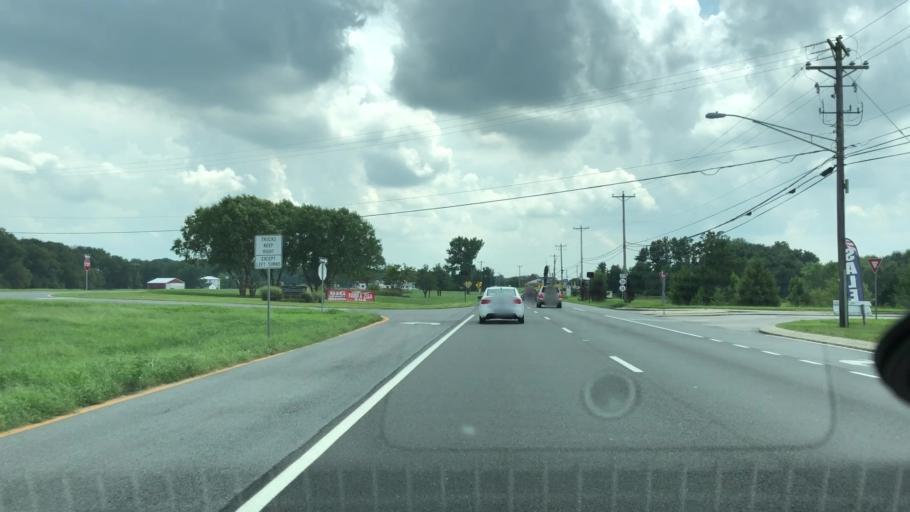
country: US
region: Delaware
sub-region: Sussex County
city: Bridgeville
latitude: 38.8106
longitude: -75.5850
